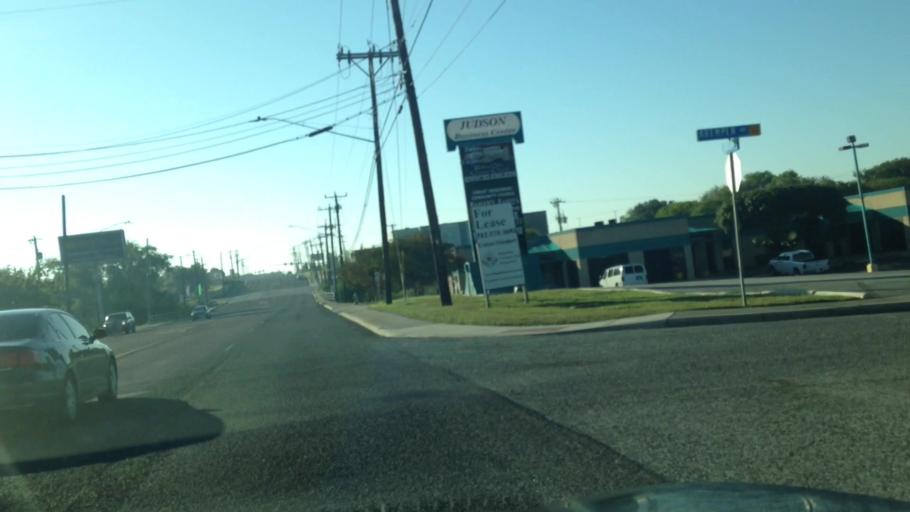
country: US
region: Texas
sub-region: Bexar County
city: Live Oak
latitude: 29.5656
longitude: -98.3644
